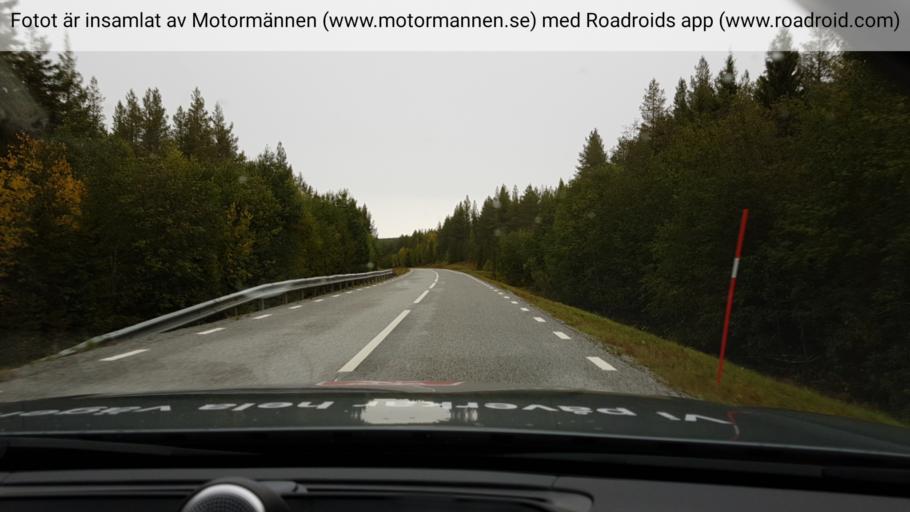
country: SE
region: Jaemtland
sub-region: Stroemsunds Kommun
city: Stroemsund
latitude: 63.9887
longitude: 15.5050
